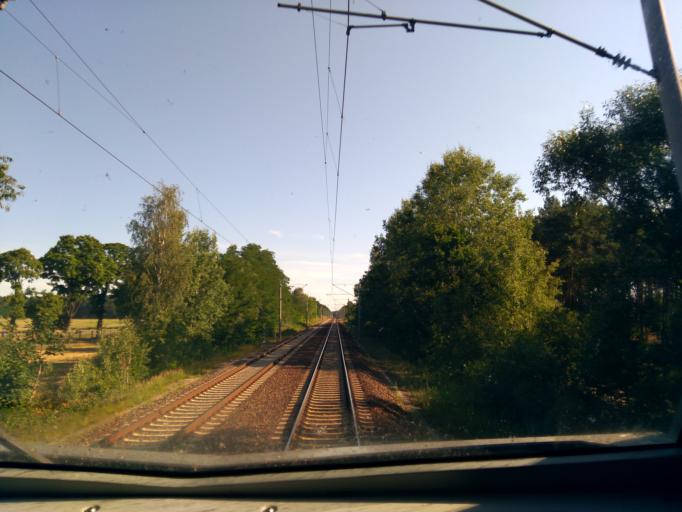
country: DE
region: Brandenburg
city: Halbe
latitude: 52.0576
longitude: 13.7227
